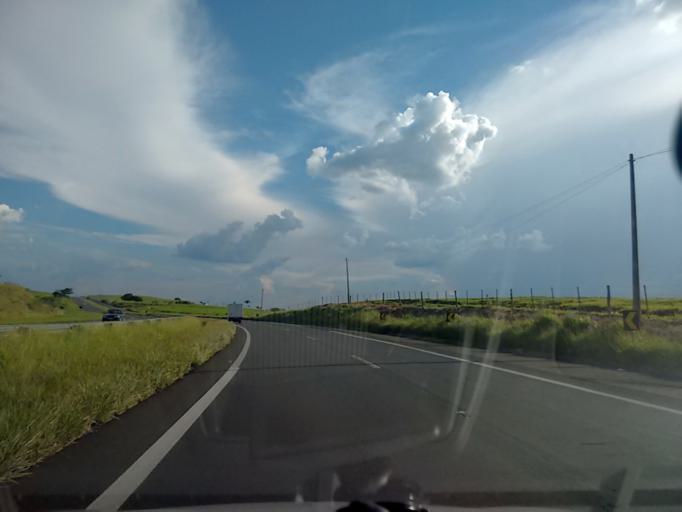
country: BR
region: Sao Paulo
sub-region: Duartina
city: Duartina
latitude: -22.2940
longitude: -49.4963
